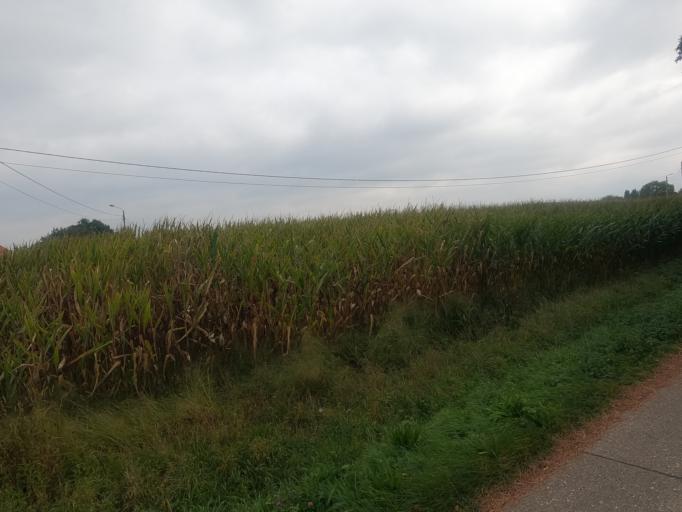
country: BE
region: Flanders
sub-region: Provincie Antwerpen
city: Heist-op-den-Berg
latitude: 51.1139
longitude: 4.7103
